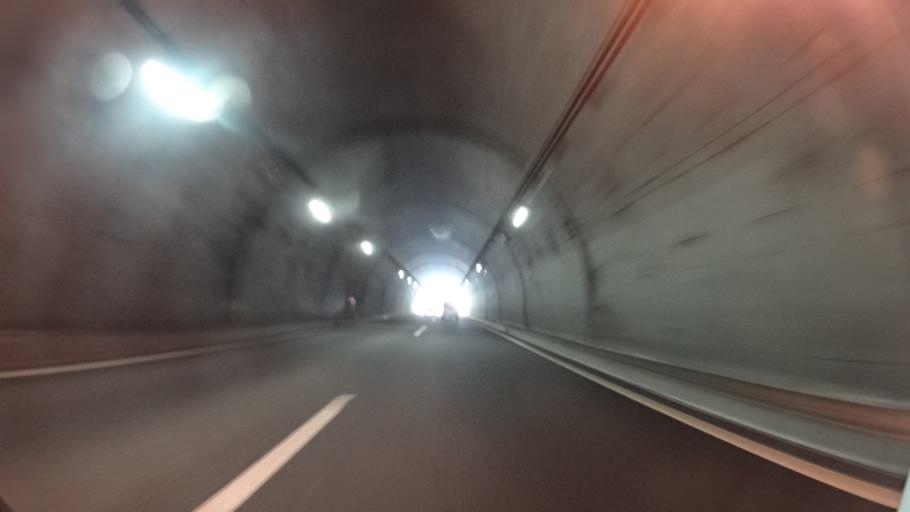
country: JP
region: Ehime
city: Saijo
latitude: 33.8863
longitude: 133.1546
